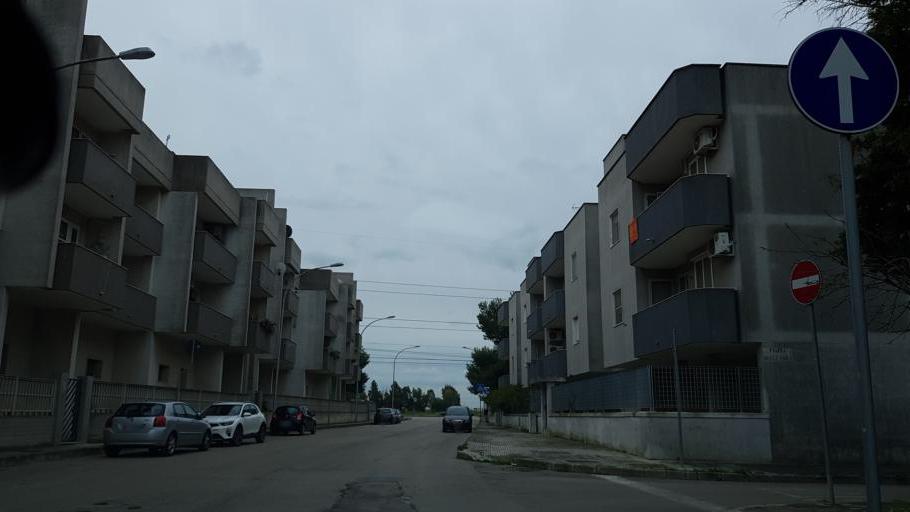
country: IT
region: Apulia
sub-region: Provincia di Brindisi
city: La Rosa
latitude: 40.6042
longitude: 17.9518
